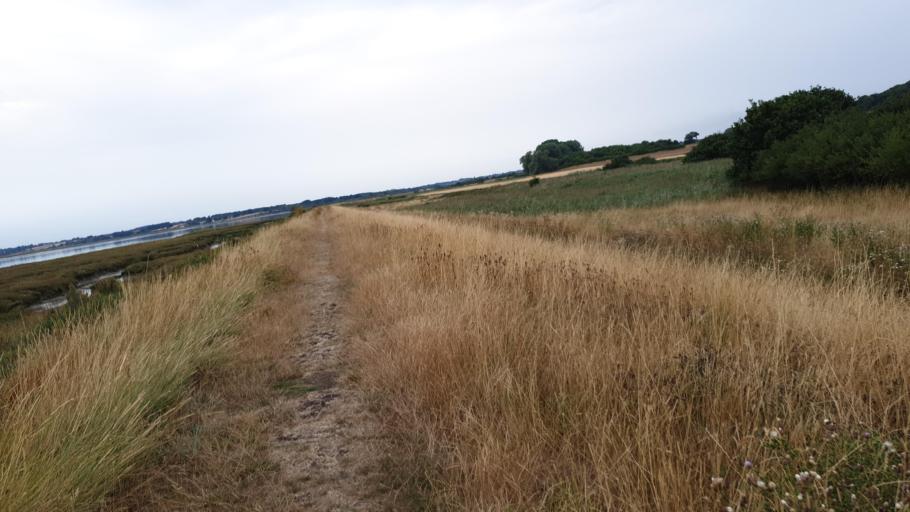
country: GB
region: England
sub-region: Essex
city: Brightlingsea
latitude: 51.8170
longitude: 0.9953
